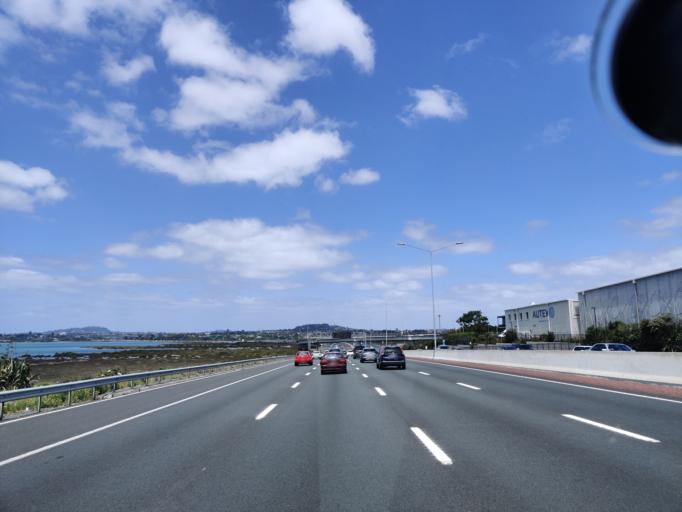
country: NZ
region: Auckland
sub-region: Auckland
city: Rosebank
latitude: -36.8685
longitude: 174.6713
